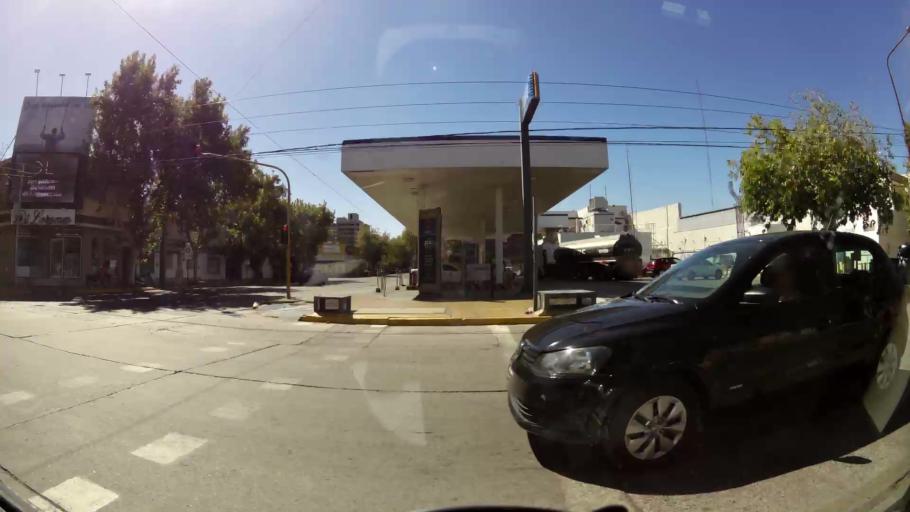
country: AR
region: San Juan
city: San Juan
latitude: -31.5379
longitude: -68.5348
